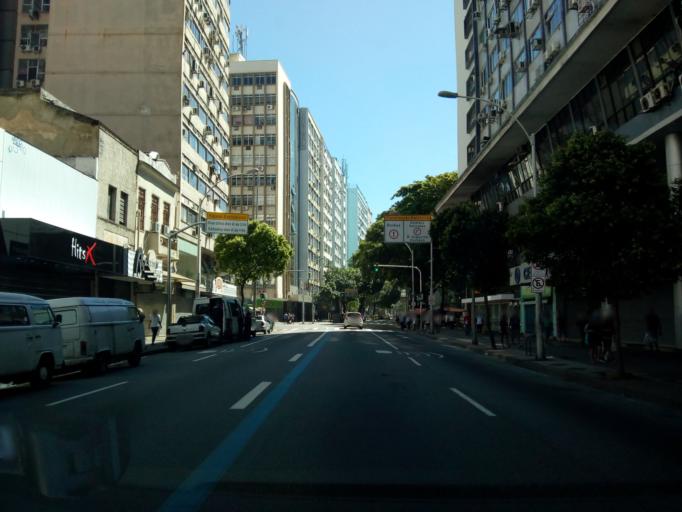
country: BR
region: Rio de Janeiro
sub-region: Rio De Janeiro
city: Rio de Janeiro
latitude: -22.9696
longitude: -43.1851
